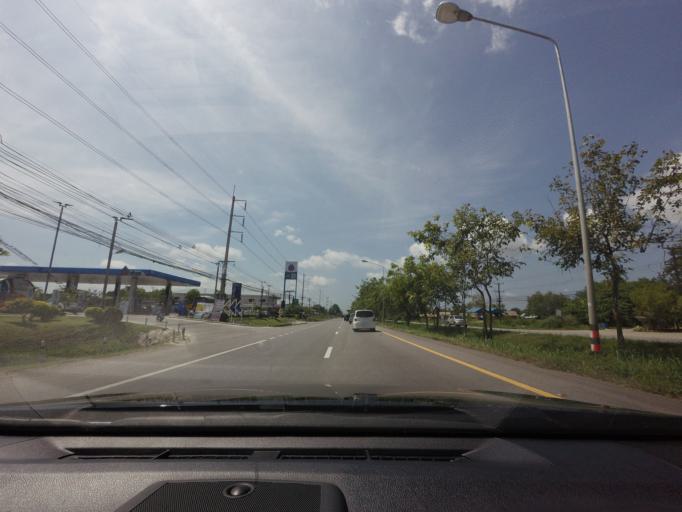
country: TH
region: Chumphon
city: Chumphon
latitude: 10.4778
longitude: 99.1261
